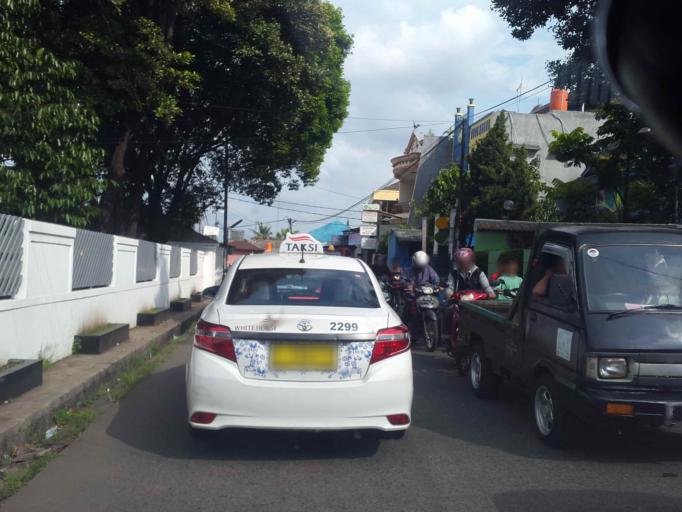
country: ID
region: West Java
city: Bekasi
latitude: -6.2769
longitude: 106.9151
